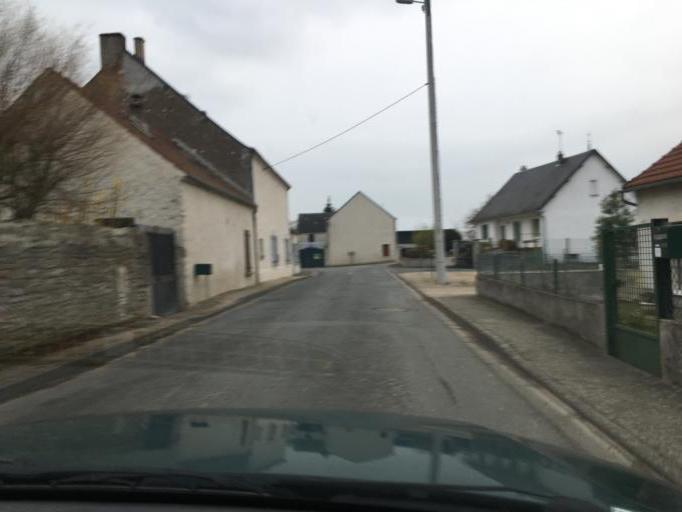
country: FR
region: Centre
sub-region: Departement du Loiret
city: Baule
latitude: 47.8175
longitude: 1.6595
